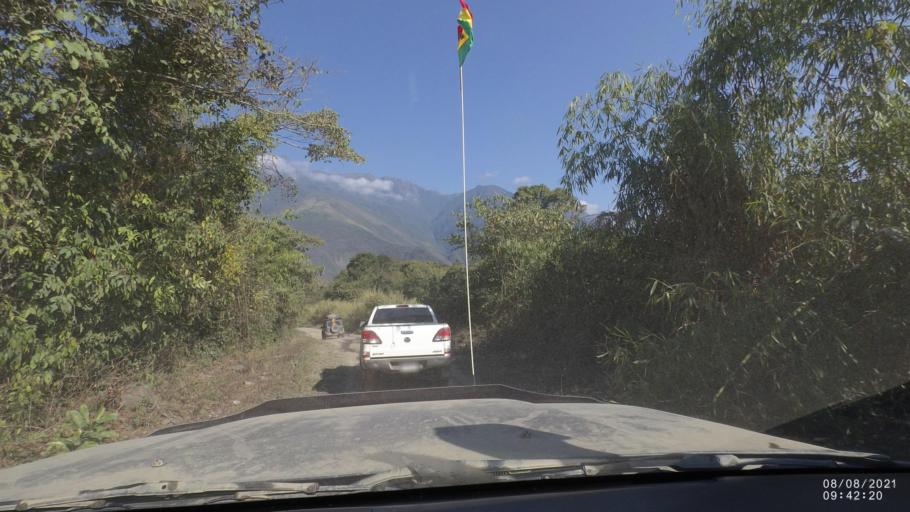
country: BO
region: La Paz
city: Quime
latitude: -16.6010
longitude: -66.7163
